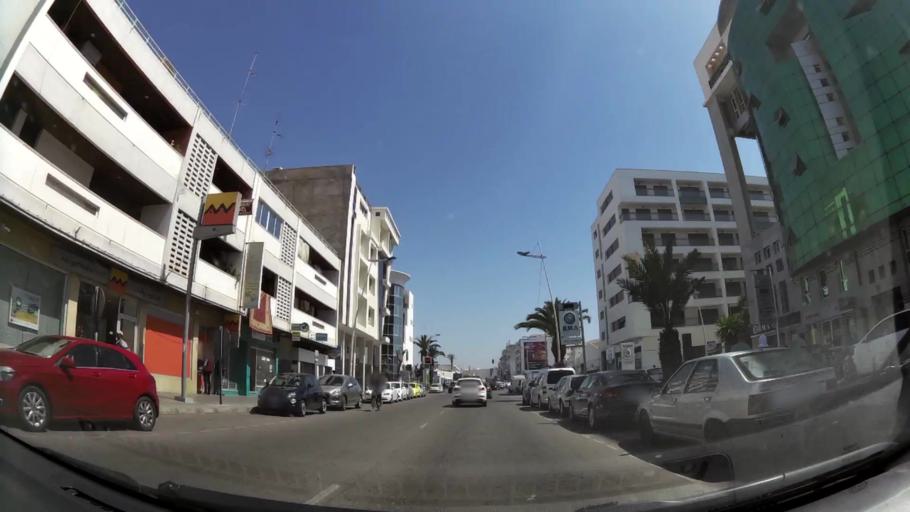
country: MA
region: Souss-Massa-Draa
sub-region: Agadir-Ida-ou-Tnan
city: Agadir
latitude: 30.4128
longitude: -9.5920
